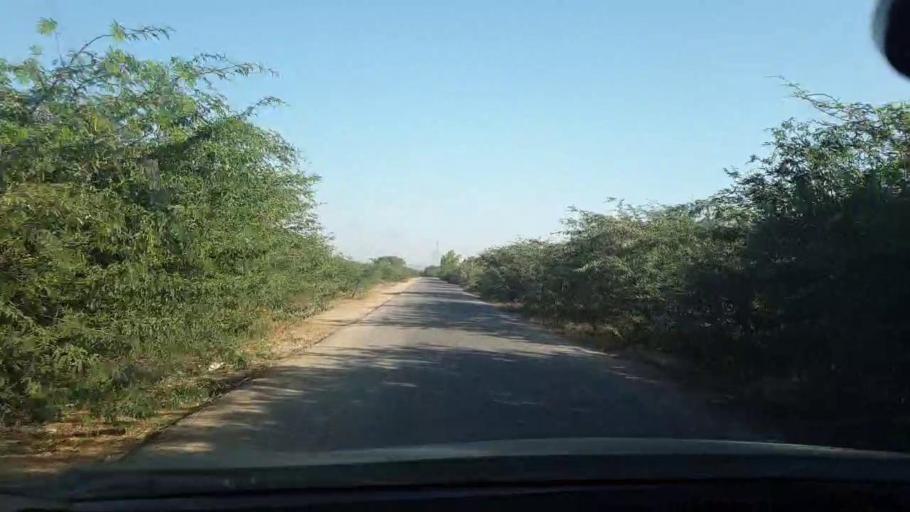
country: PK
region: Sindh
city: Malir Cantonment
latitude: 25.1514
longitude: 67.1899
